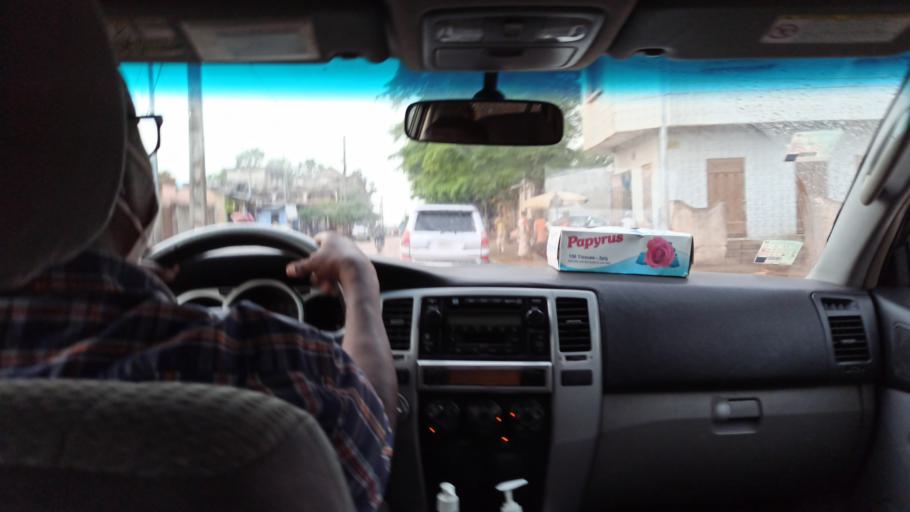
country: BJ
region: Queme
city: Porto-Novo
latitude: 6.4990
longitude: 2.6399
